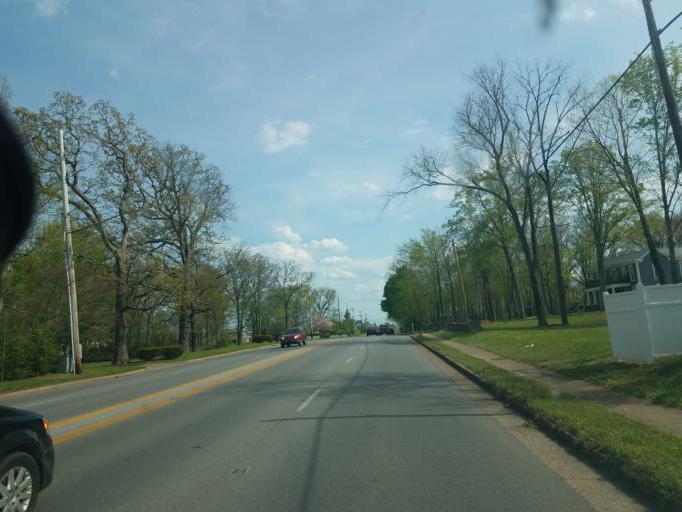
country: US
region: Kentucky
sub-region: Warren County
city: Bowling Green
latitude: 36.9742
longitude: -86.4362
